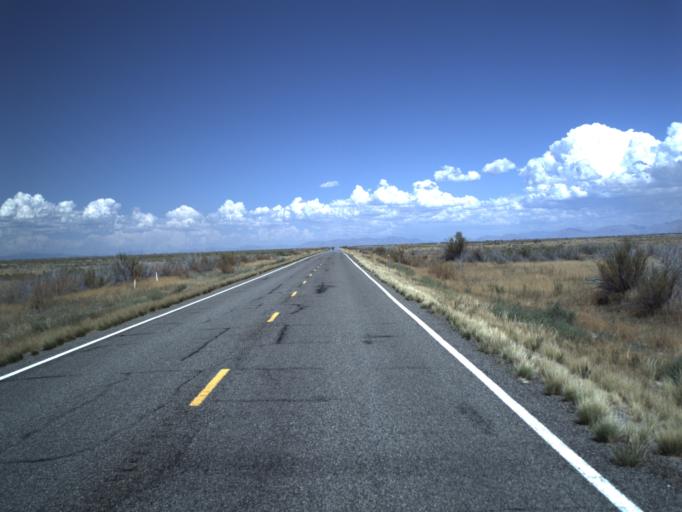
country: US
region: Utah
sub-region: Millard County
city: Delta
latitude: 39.2893
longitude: -112.8303
